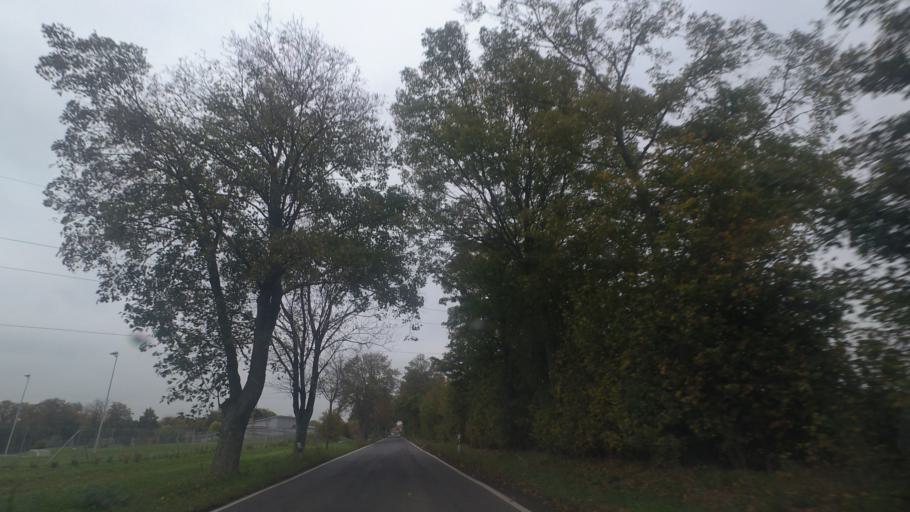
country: DE
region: Rheinland-Pfalz
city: Undenheim
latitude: 49.8354
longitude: 8.2136
